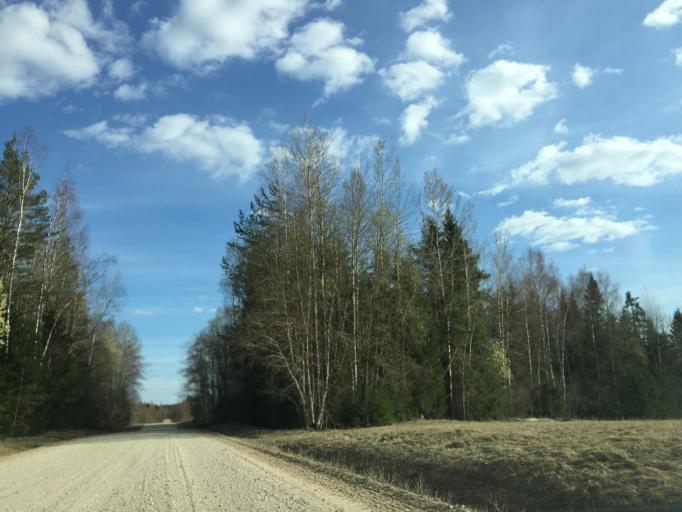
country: EE
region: Tartu
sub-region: Elva linn
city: Elva
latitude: 58.1212
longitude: 26.5279
